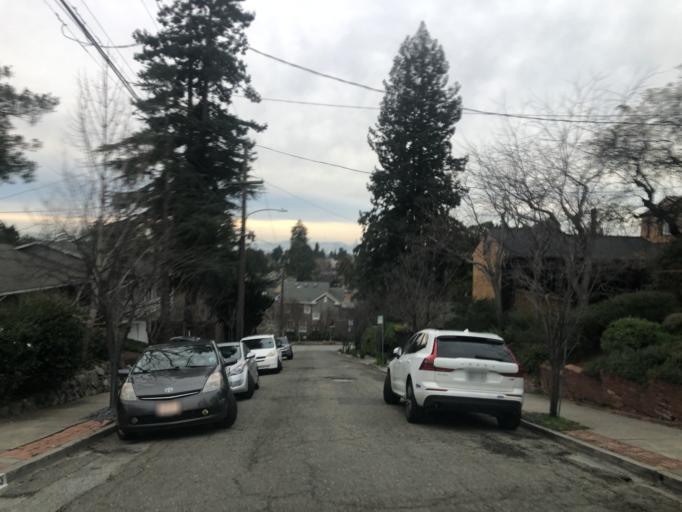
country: US
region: California
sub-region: Alameda County
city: Piedmont
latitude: 37.8502
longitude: -122.2465
